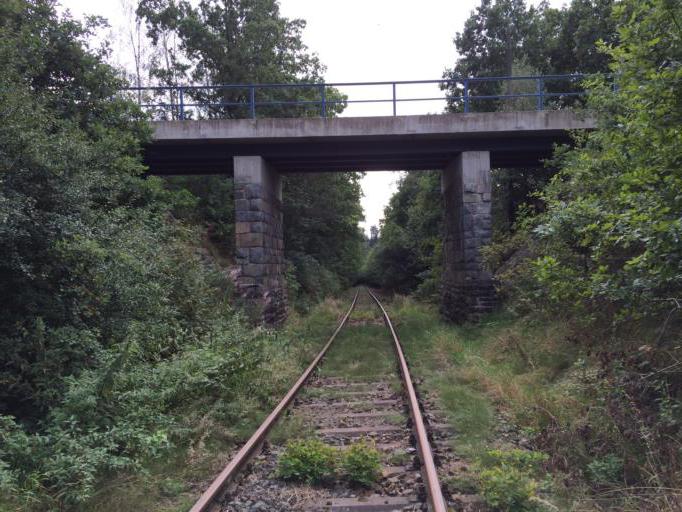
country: DE
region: Thuringia
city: Bucha
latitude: 50.6446
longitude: 11.7026
